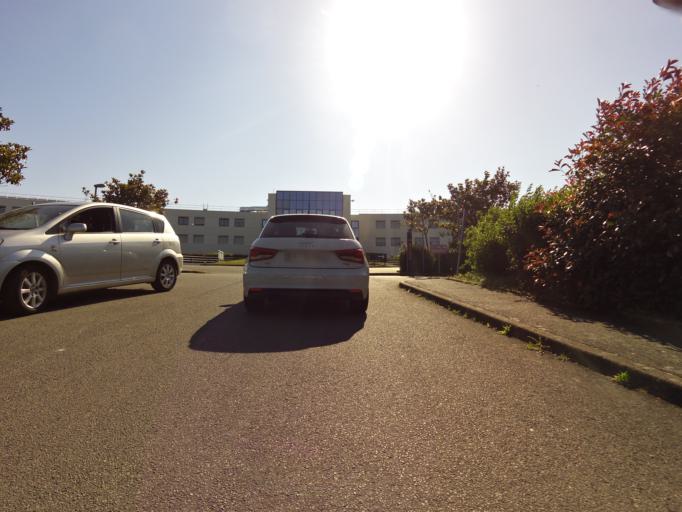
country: FR
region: Pays de la Loire
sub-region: Departement de la Loire-Atlantique
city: Saint-Herblain
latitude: 47.2268
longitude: -1.6118
